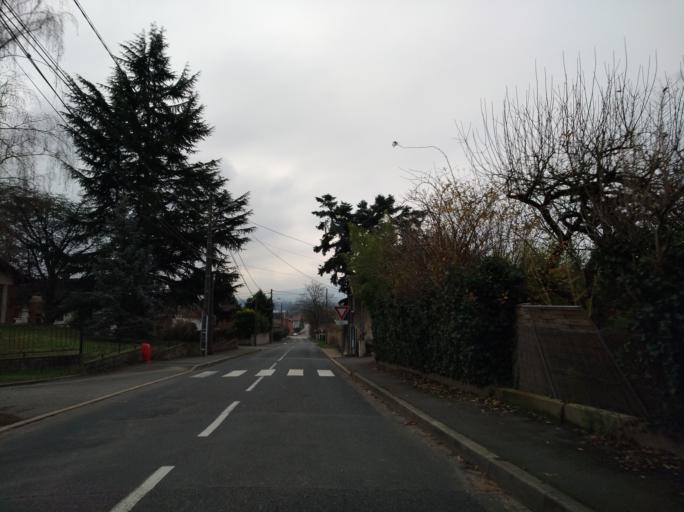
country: FR
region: Rhone-Alpes
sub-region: Departement de l'Ain
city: Reyrieux
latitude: 45.9382
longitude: 4.8113
